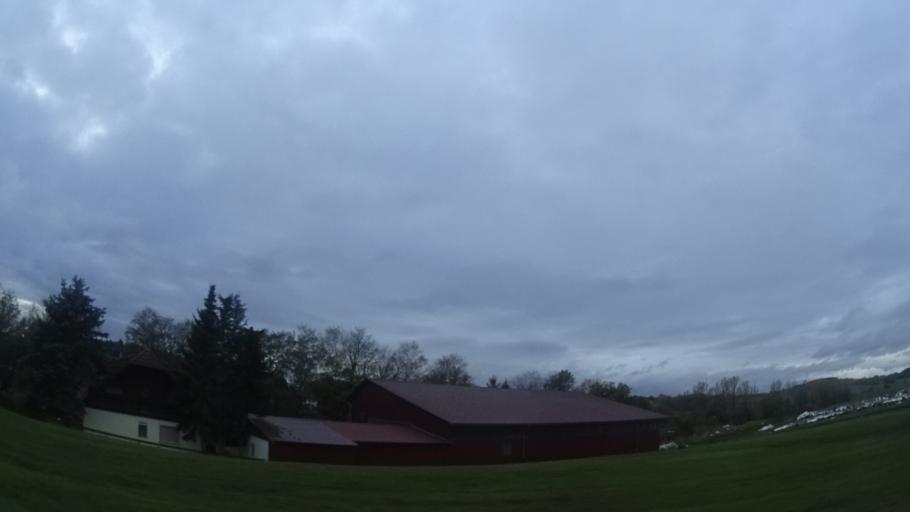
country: DE
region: Hesse
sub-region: Regierungsbezirk Giessen
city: Freiensteinau
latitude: 50.3750
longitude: 9.4267
